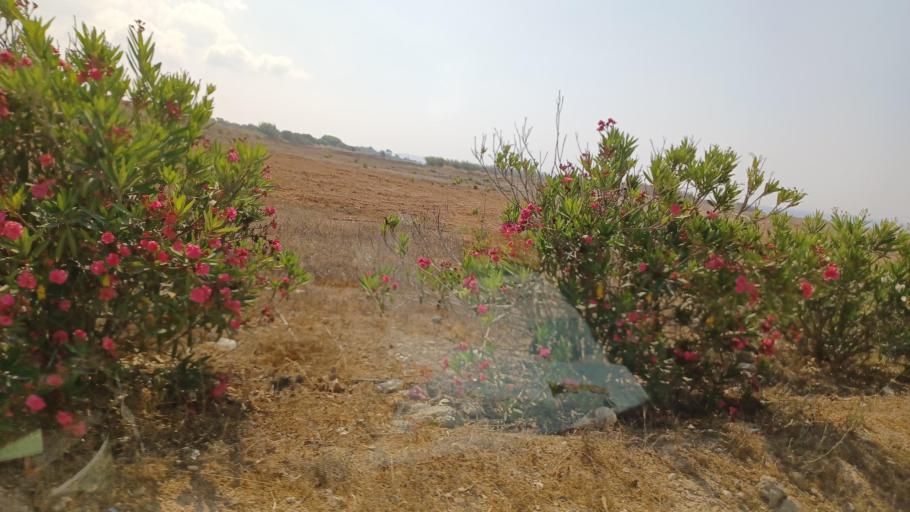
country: CY
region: Larnaka
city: Xylotymbou
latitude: 34.9789
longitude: 33.7826
